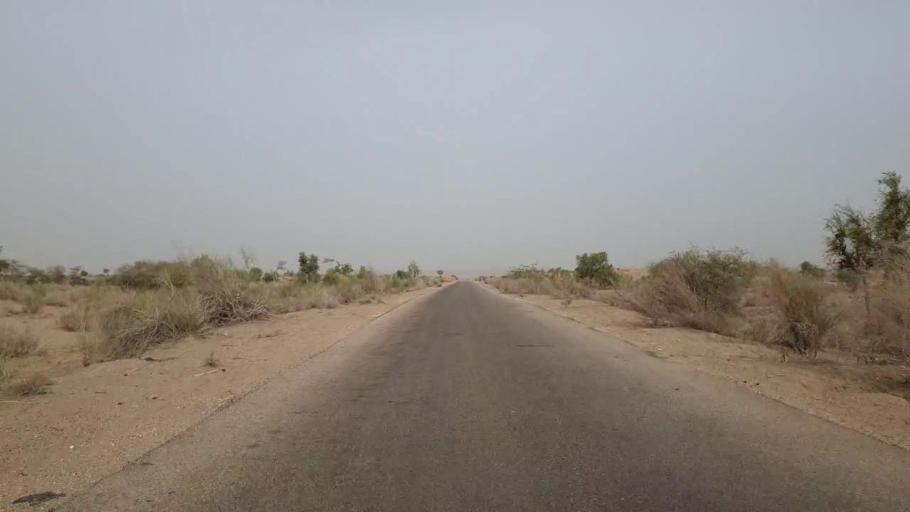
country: PK
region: Sindh
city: Islamkot
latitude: 24.5575
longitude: 70.3461
